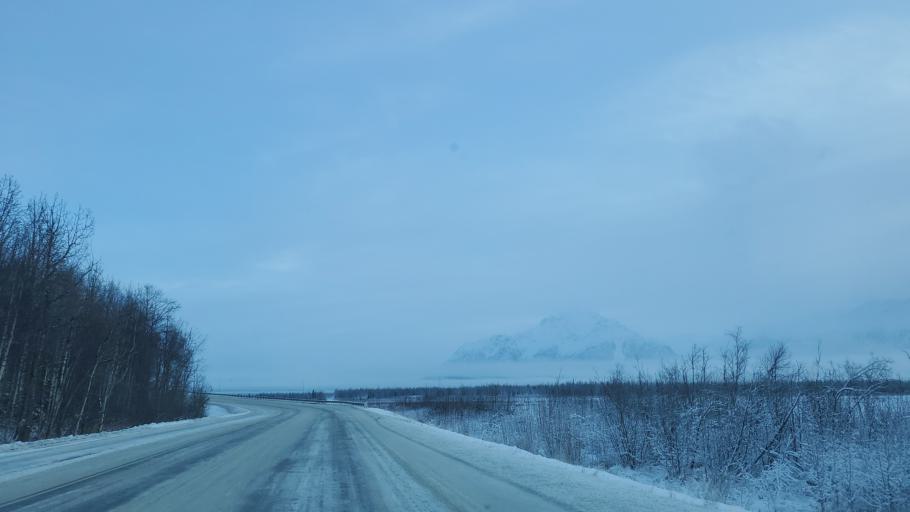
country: US
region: Alaska
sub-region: Matanuska-Susitna Borough
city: Gateway
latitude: 61.5501
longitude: -149.2862
